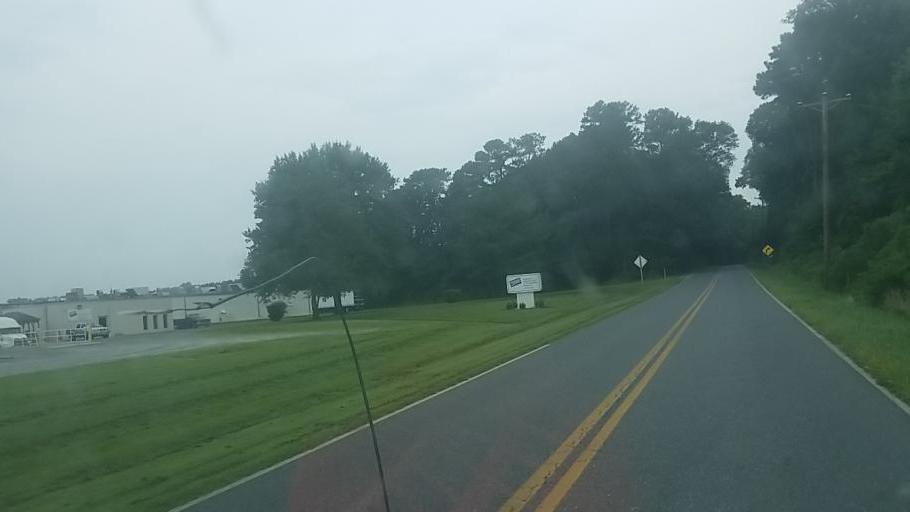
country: US
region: Maryland
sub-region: Wicomico County
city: Salisbury
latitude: 38.3859
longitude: -75.5279
